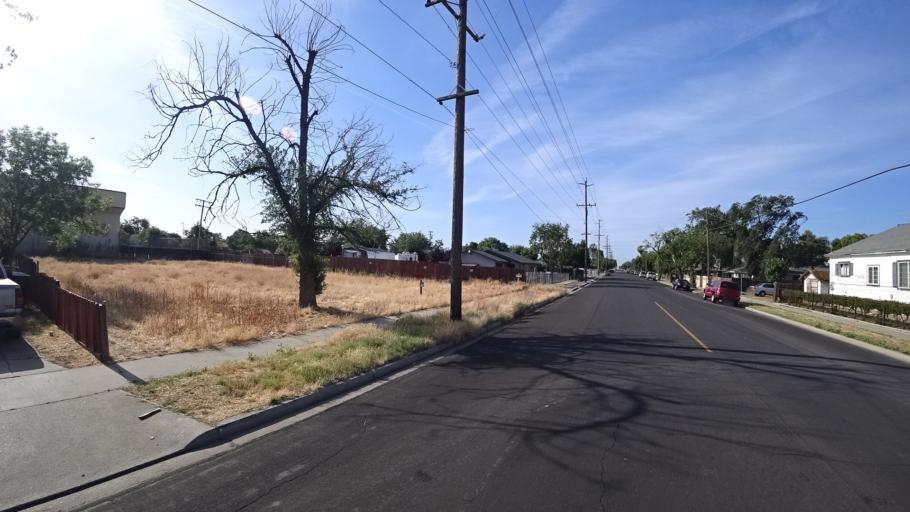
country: US
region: California
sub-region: Kings County
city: Hanford
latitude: 36.3198
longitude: -119.6460
